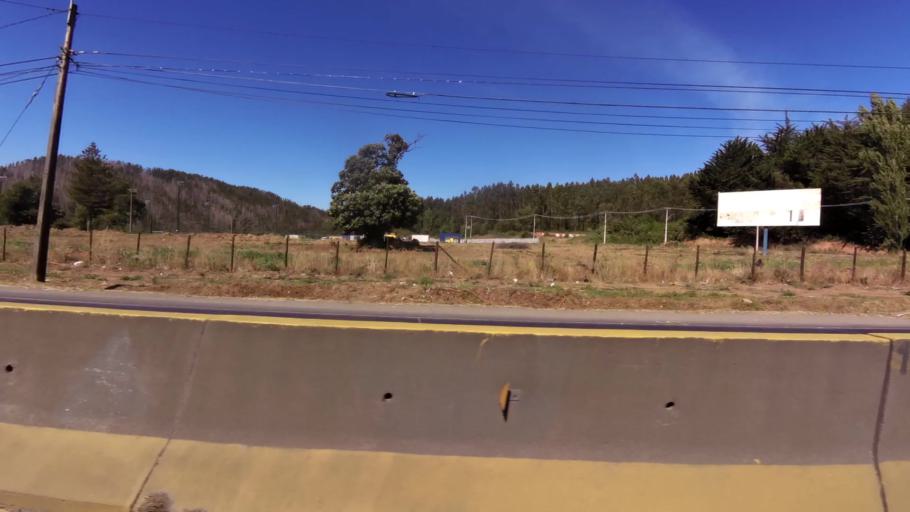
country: CL
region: Biobio
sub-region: Provincia de Concepcion
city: Concepcion
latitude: -36.7985
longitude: -73.0258
